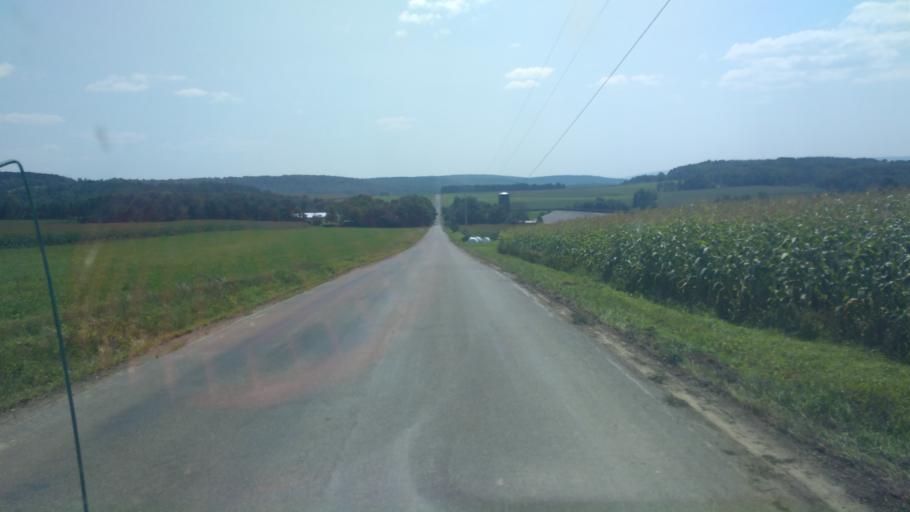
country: US
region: New York
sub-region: Steuben County
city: Canisteo
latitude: 42.3473
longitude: -77.5776
